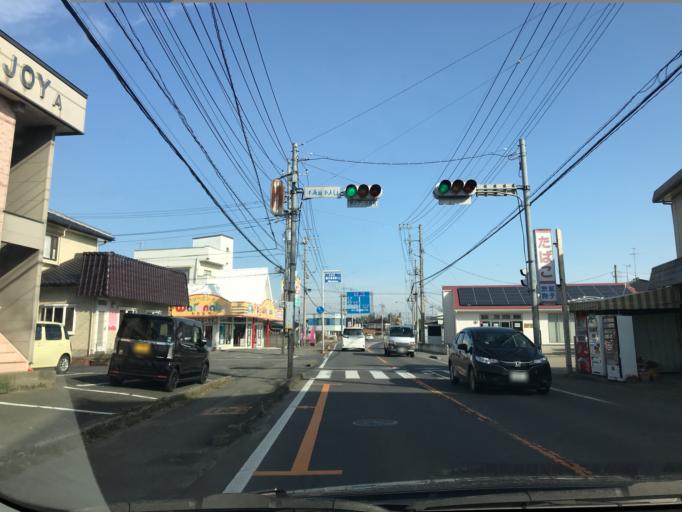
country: JP
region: Ibaraki
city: Mitsukaido
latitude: 36.0342
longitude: 139.9879
